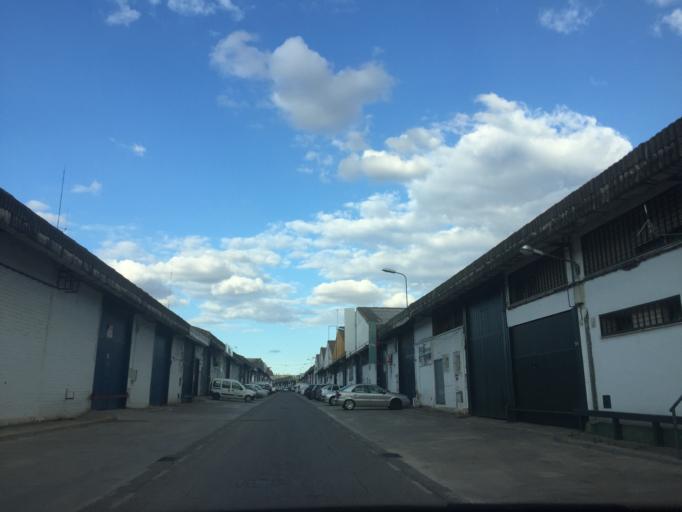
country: ES
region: Andalusia
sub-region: Provincia de Sevilla
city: Sevilla
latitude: 37.3649
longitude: -5.9599
